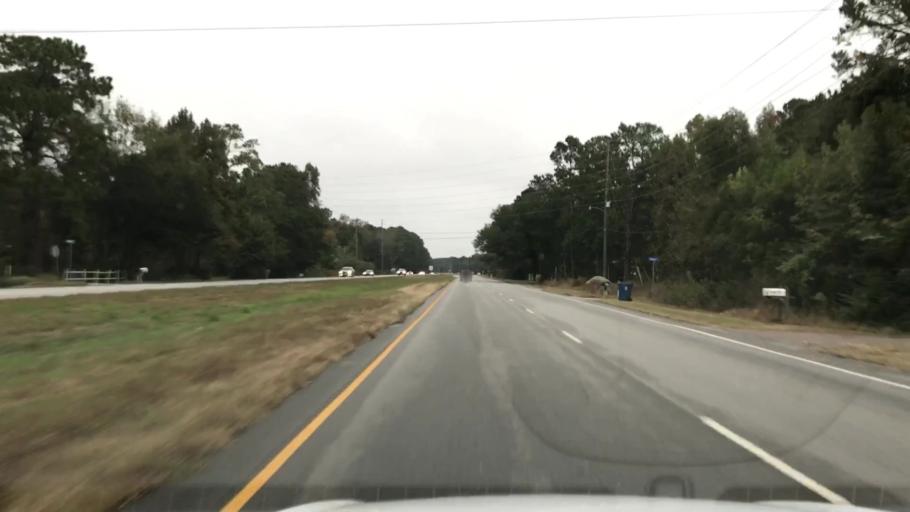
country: US
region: South Carolina
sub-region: Charleston County
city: Isle of Palms
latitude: 32.8933
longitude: -79.7376
